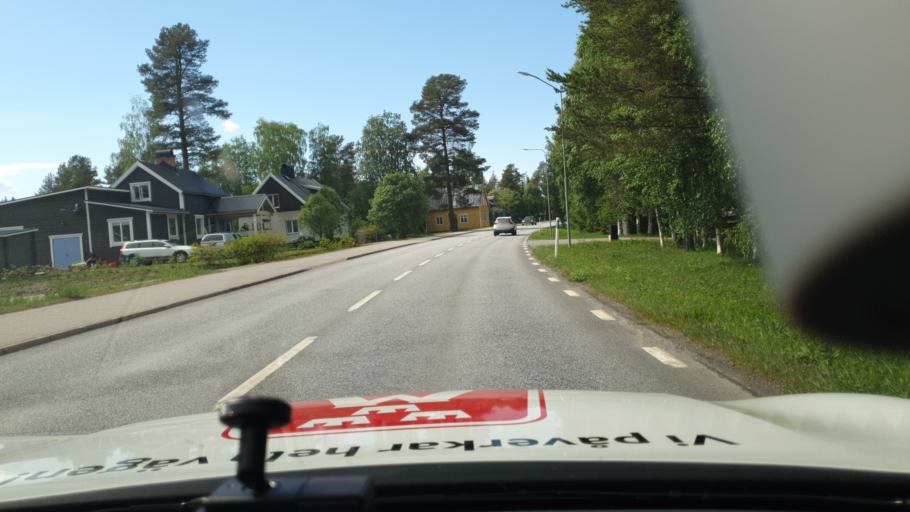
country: SE
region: Vaesterbotten
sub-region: Storumans Kommun
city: Storuman
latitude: 65.0709
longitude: 17.1385
